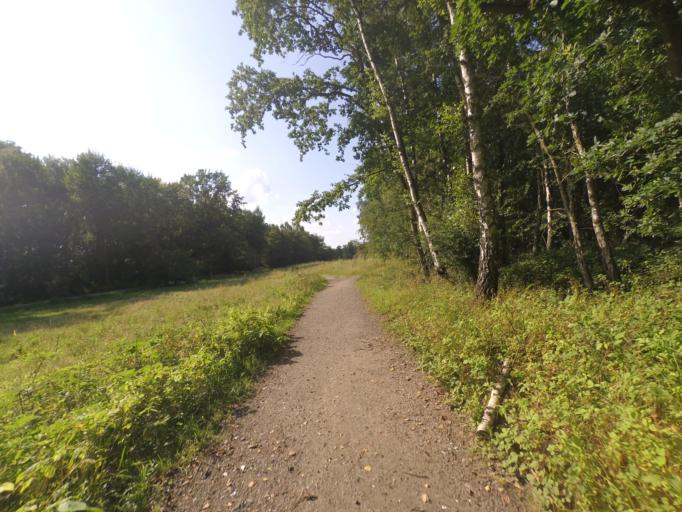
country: DE
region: Schleswig-Holstein
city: Oststeinbek
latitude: 53.5076
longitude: 10.1674
